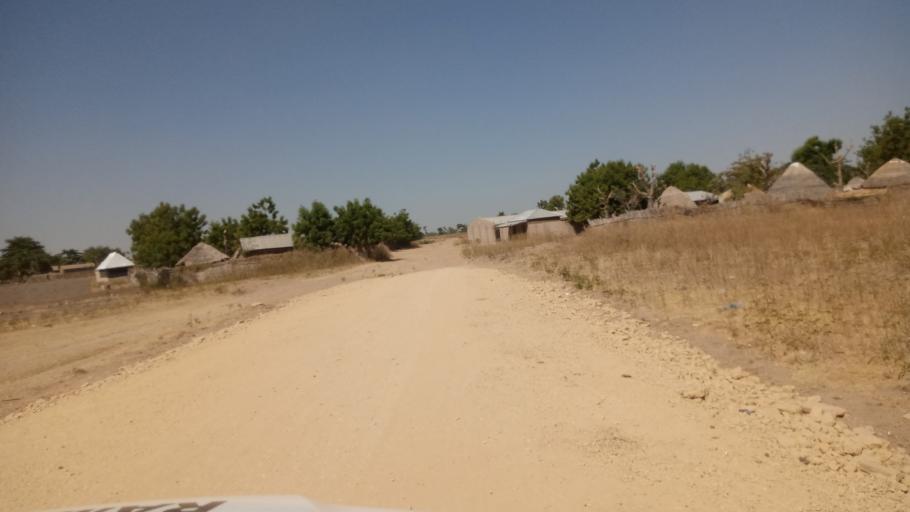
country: NG
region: Adamawa
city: Ngurore
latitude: 9.2981
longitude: 12.1369
